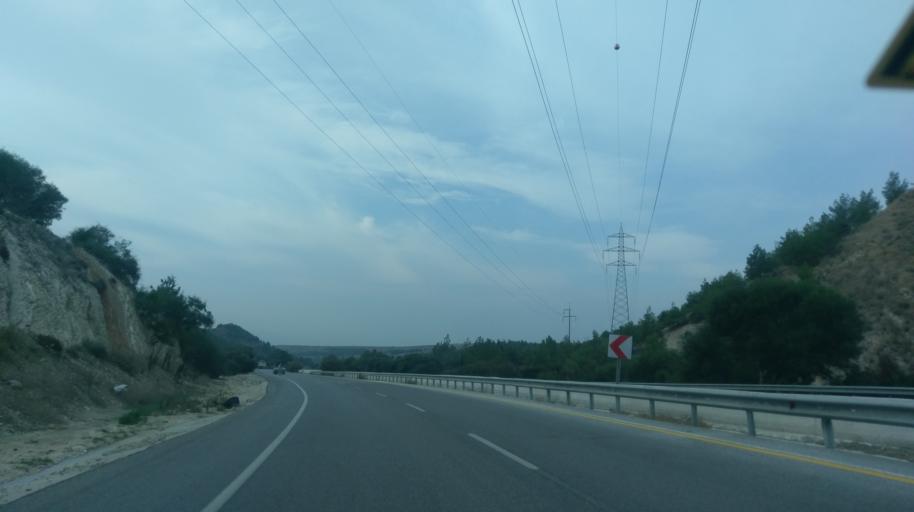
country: CY
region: Lefkosia
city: Akaki
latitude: 35.2114
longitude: 33.1256
